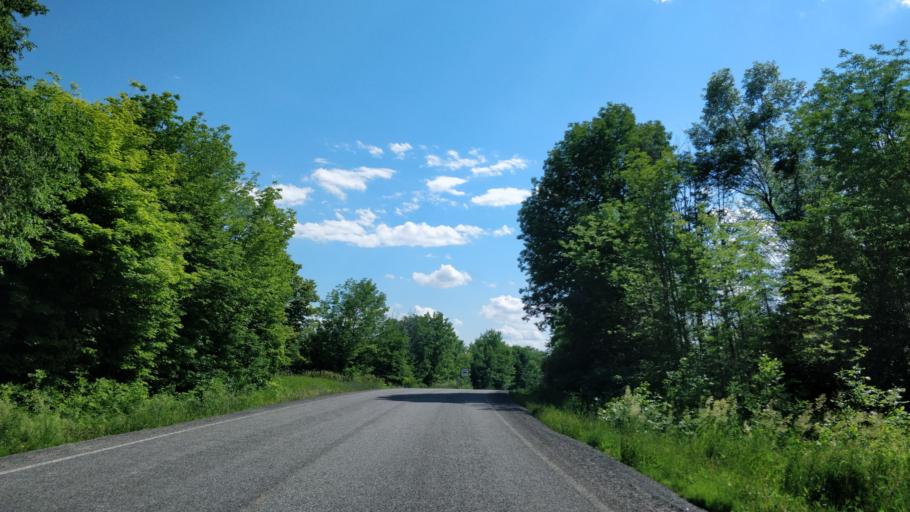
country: CA
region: Ontario
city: Perth
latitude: 44.7629
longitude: -76.4651
